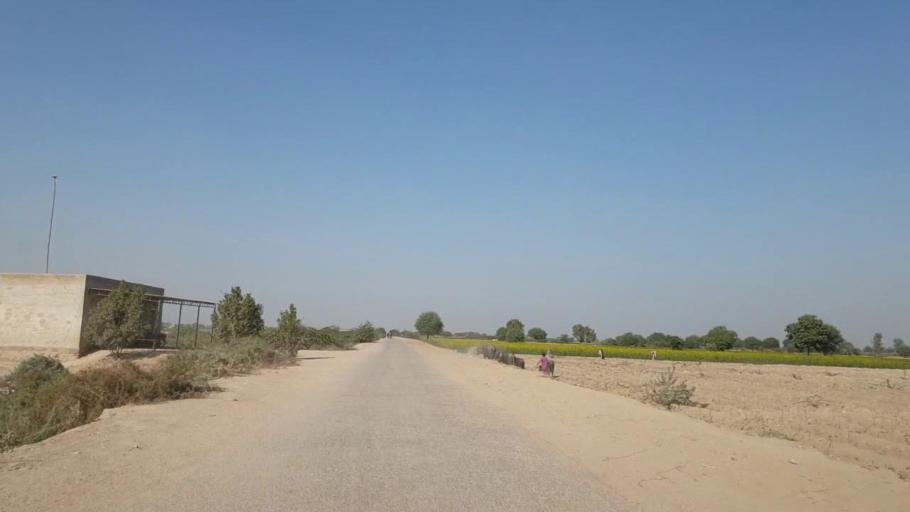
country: PK
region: Sindh
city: Digri
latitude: 25.0128
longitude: 69.1060
